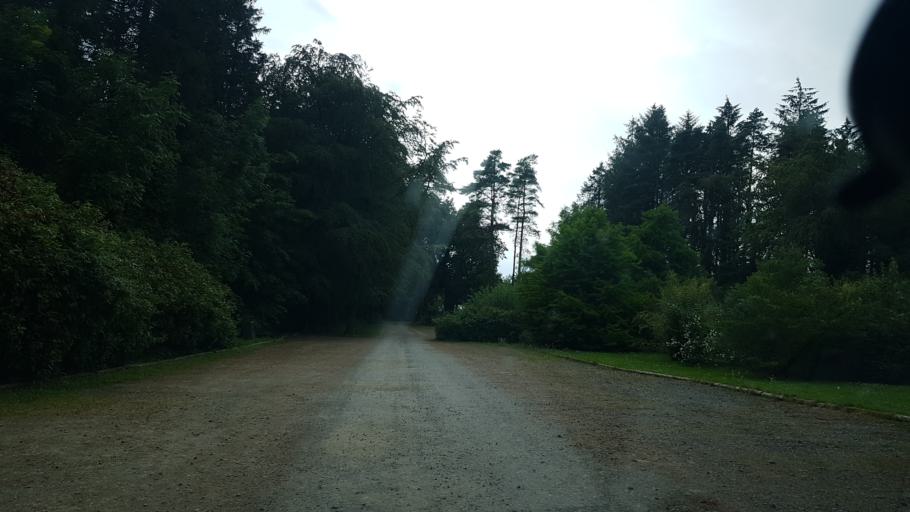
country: GB
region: Wales
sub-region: Pembrokeshire
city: Wiston
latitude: 51.7852
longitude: -4.8870
